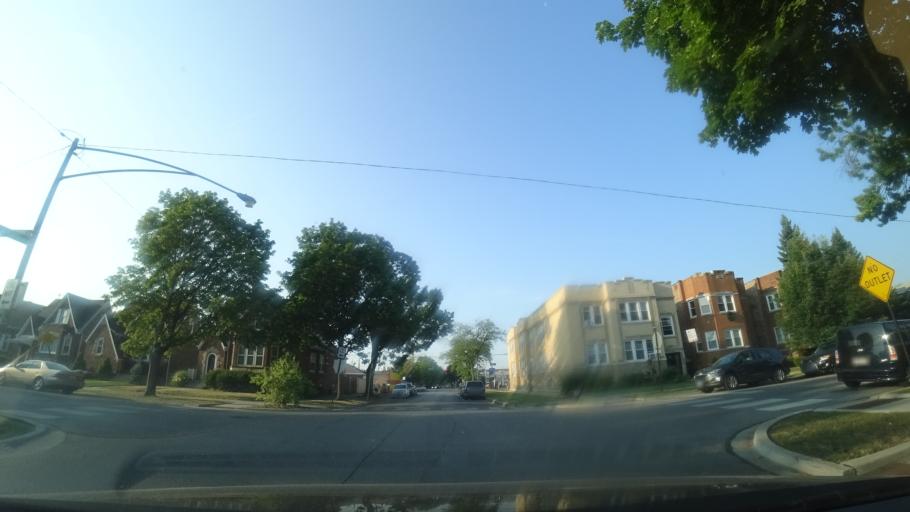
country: US
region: Illinois
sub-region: Cook County
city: Elmwood Park
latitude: 41.9395
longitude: -87.7713
